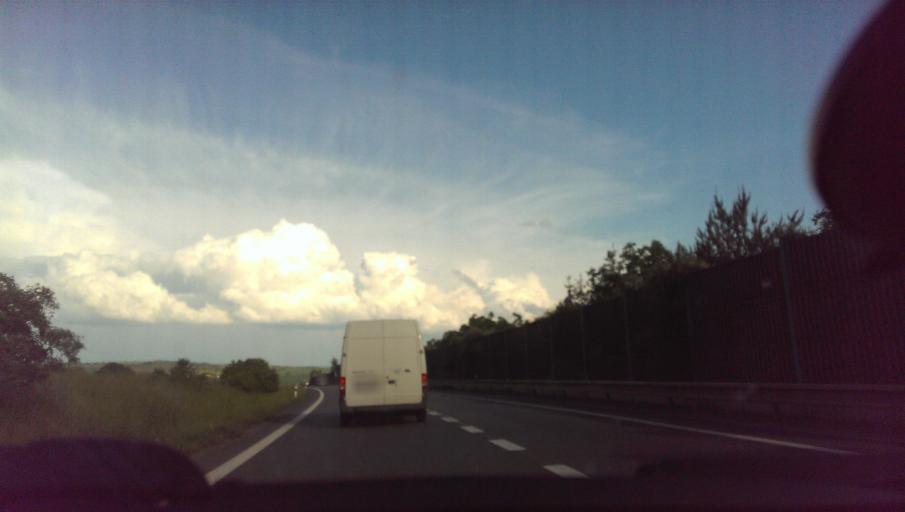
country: CZ
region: South Moravian
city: Blazovice
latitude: 49.1805
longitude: 16.8110
